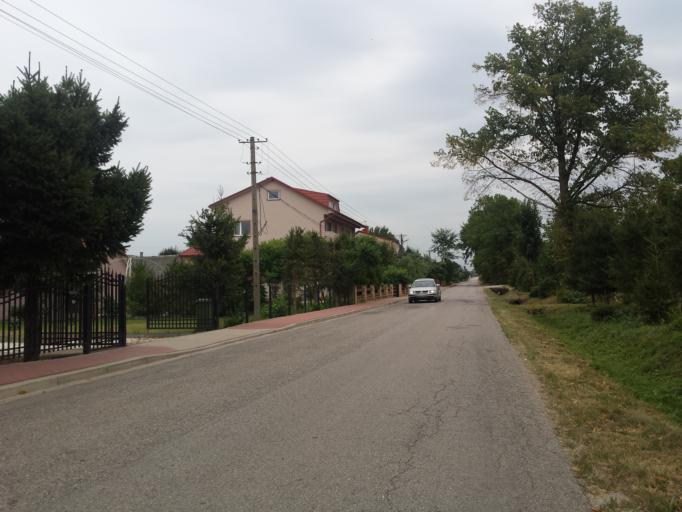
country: PL
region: Swietokrzyskie
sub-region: Powiat kielecki
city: Morawica
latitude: 50.7329
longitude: 20.6765
